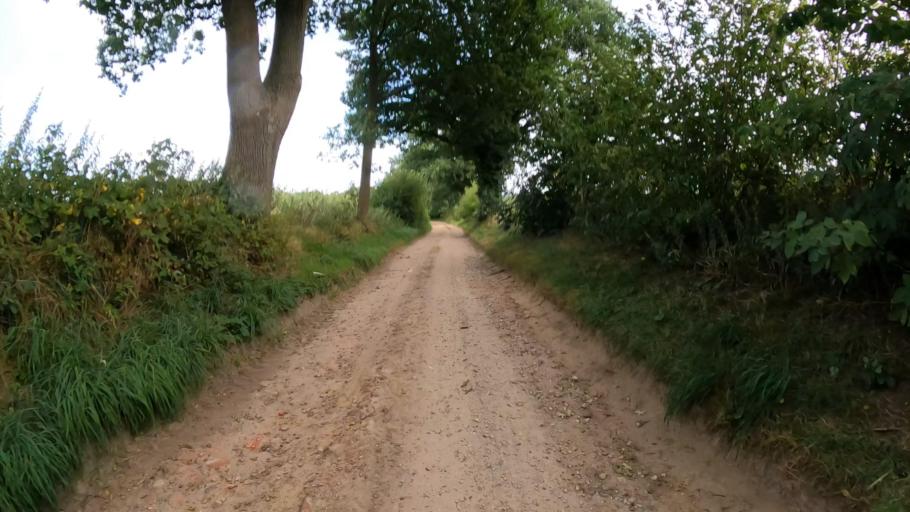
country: DE
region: Lower Saxony
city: Seevetal
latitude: 53.4157
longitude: 9.9734
